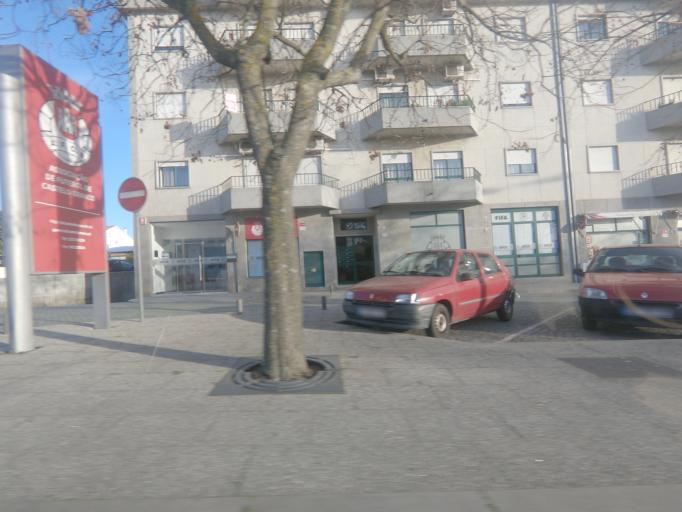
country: PT
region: Castelo Branco
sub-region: Castelo Branco
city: Castelo Branco
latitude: 39.8117
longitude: -7.5071
